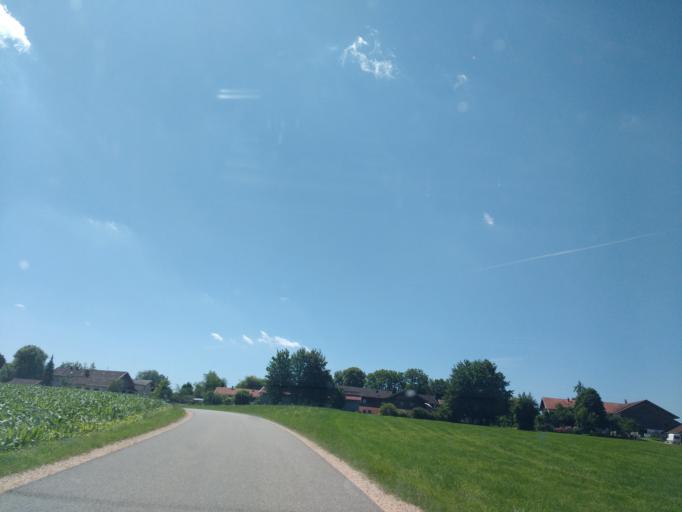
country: DE
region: Bavaria
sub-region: Upper Bavaria
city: Obing
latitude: 48.0165
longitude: 12.4410
